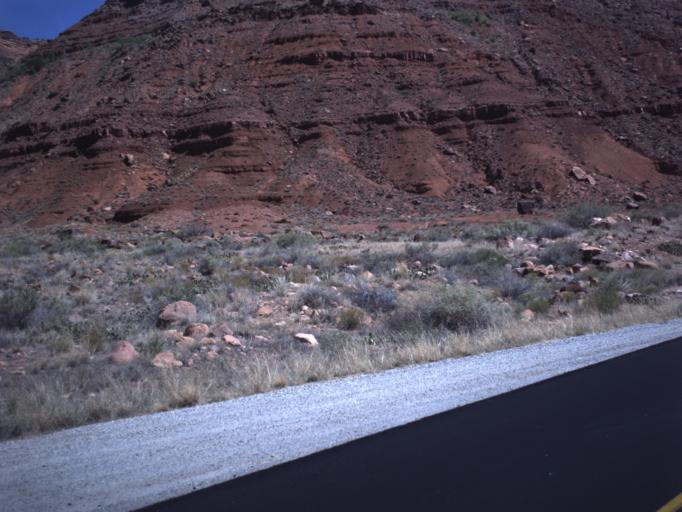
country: US
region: Utah
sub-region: Grand County
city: Moab
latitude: 38.6502
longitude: -109.4817
